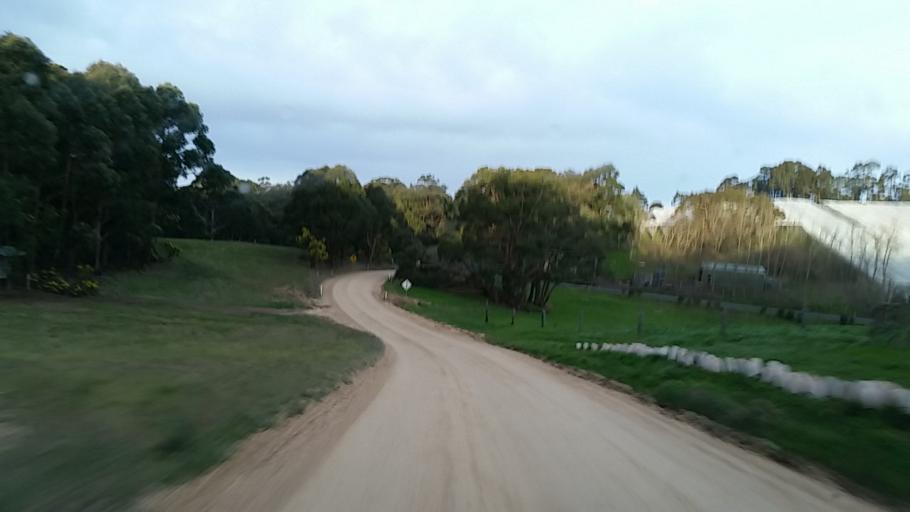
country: AU
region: South Australia
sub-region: Adelaide Hills
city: Lobethal
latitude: -34.8913
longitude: 138.8374
